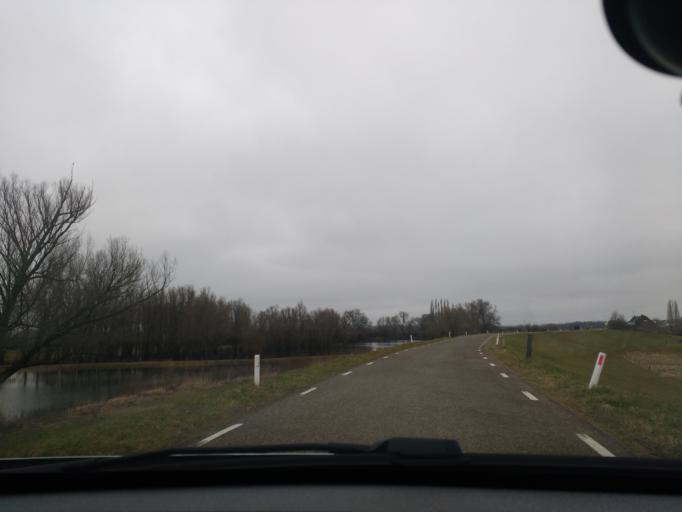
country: NL
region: Gelderland
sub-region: Gemeente Groesbeek
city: Berg en Dal
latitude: 51.8650
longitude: 5.9017
